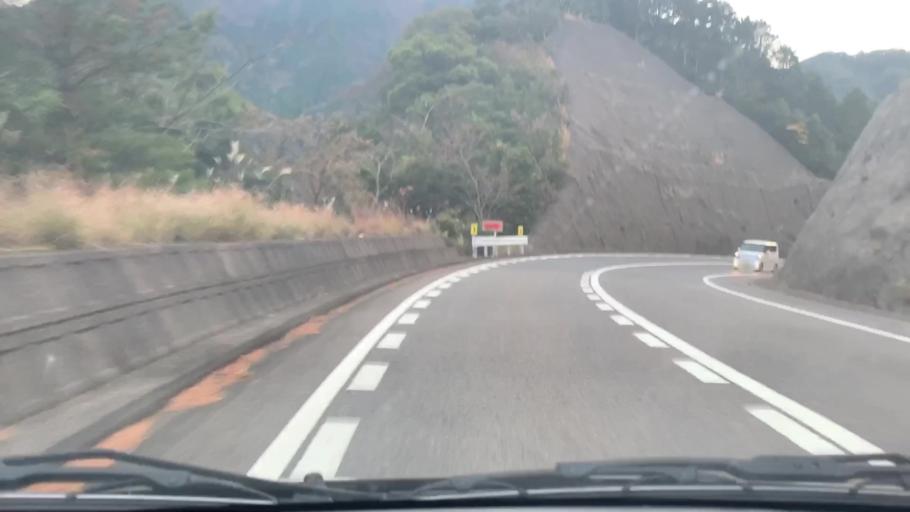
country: JP
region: Nagasaki
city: Omura
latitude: 32.9822
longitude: 130.0390
